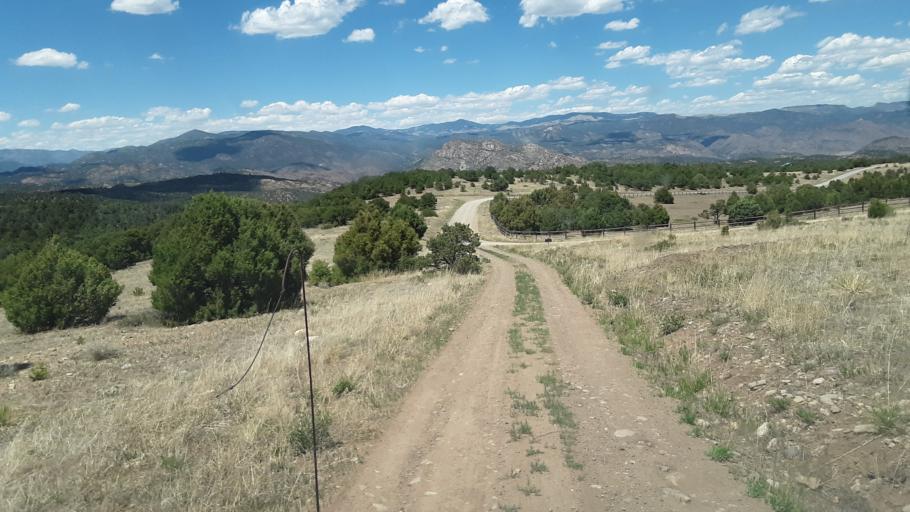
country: US
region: Colorado
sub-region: Custer County
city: Westcliffe
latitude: 38.3047
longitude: -105.6776
